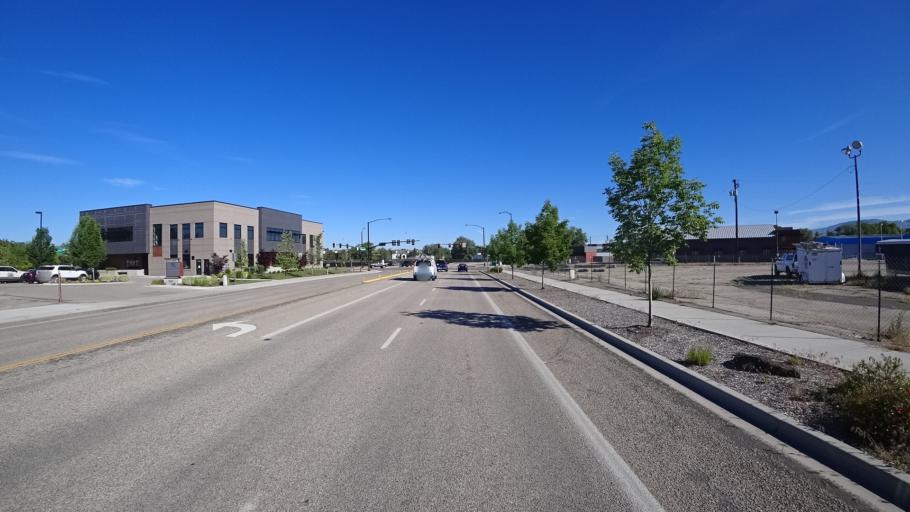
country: US
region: Idaho
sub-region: Ada County
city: Garden City
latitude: 43.6211
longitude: -116.2272
